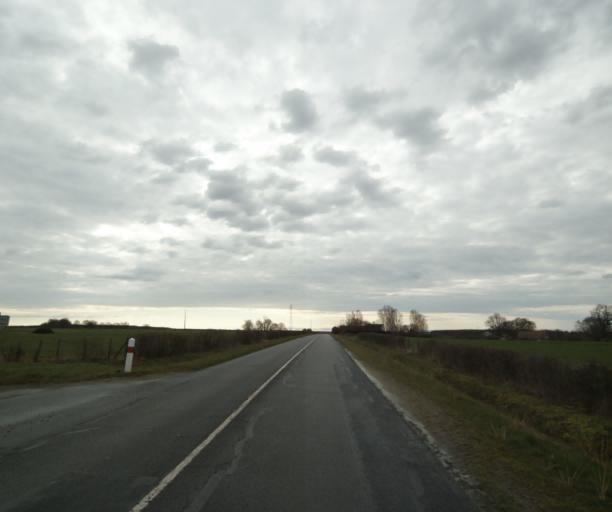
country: FR
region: Auvergne
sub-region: Departement de l'Allier
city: Toulon-sur-Allier
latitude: 46.5055
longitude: 3.3723
